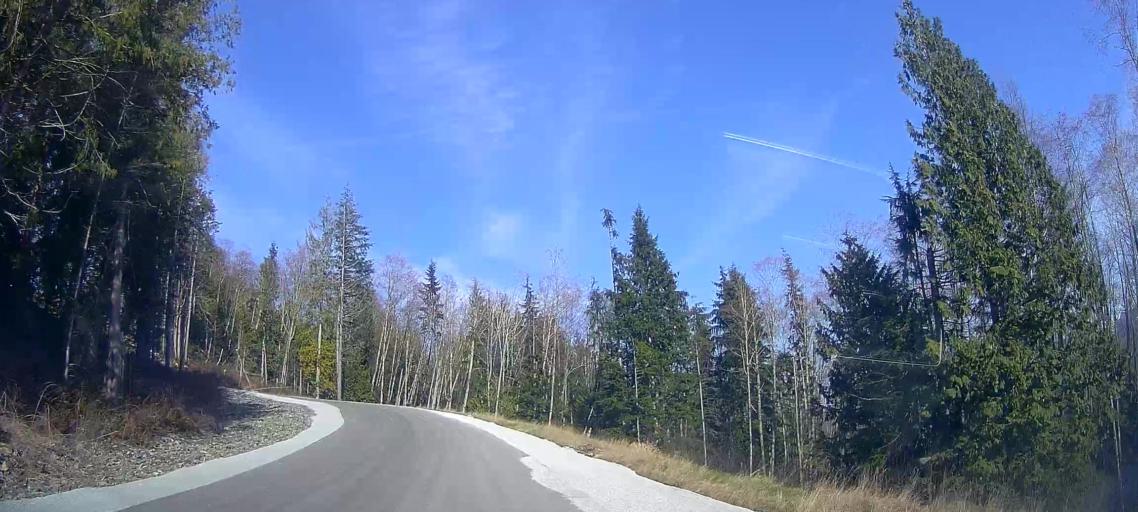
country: US
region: Washington
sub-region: Whatcom County
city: Sudden Valley
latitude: 48.5960
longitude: -122.3839
